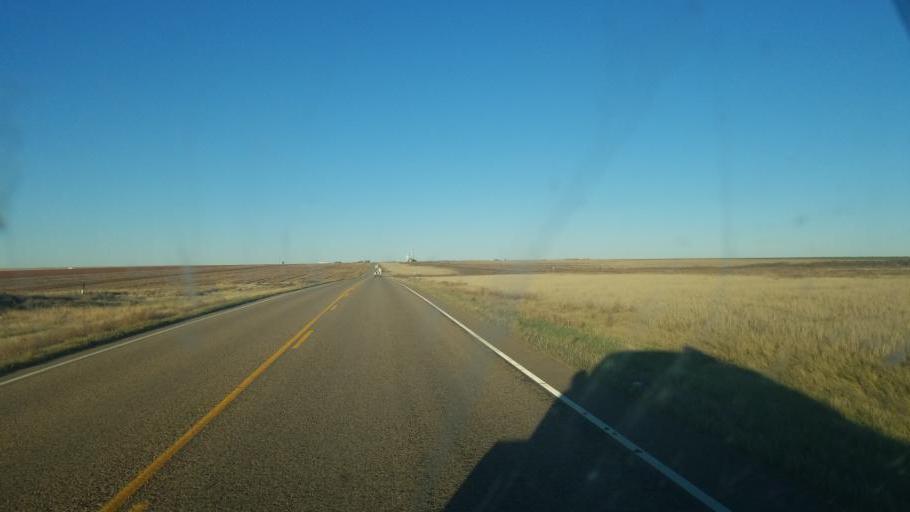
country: US
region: Colorado
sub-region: Cheyenne County
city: Cheyenne Wells
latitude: 38.8168
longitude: -102.5181
